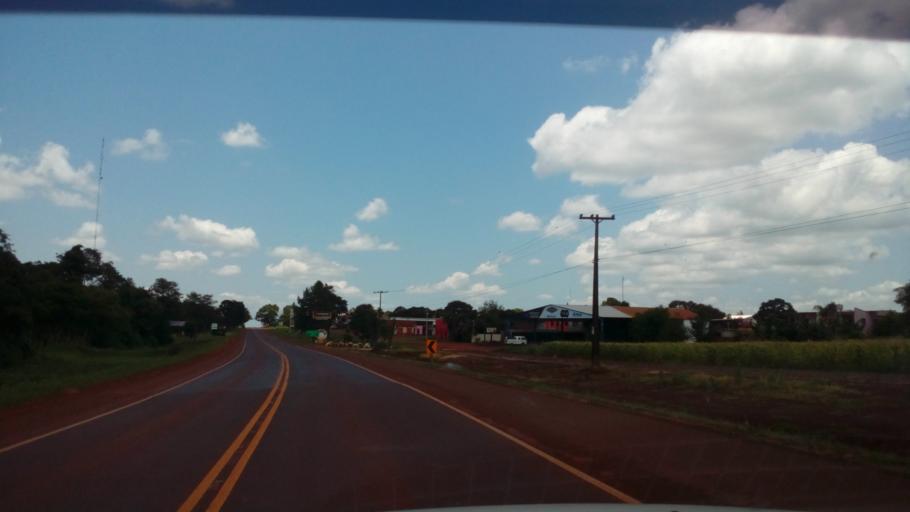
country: PY
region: Itapua
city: Arquitecto Tomas Romero Pereira
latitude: -26.3626
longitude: -55.2413
